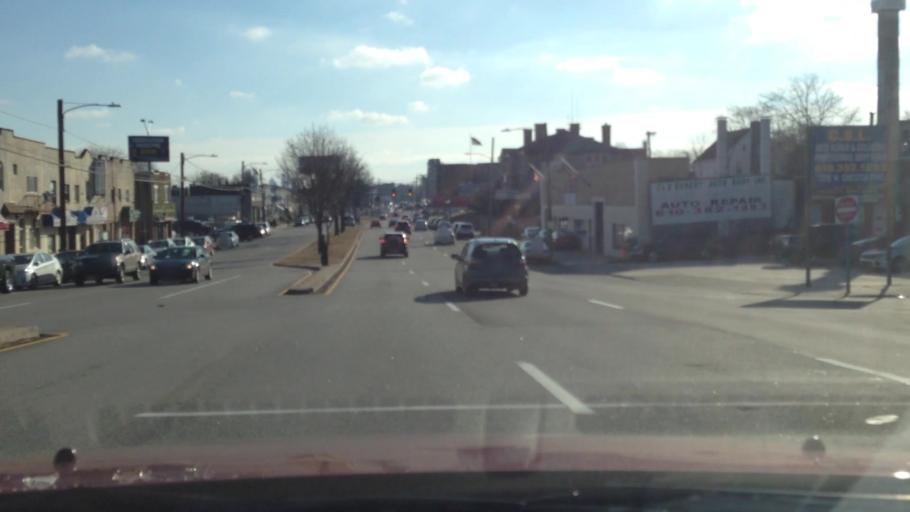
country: US
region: Pennsylvania
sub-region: Delaware County
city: Millbourne
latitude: 39.9635
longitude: -75.2681
